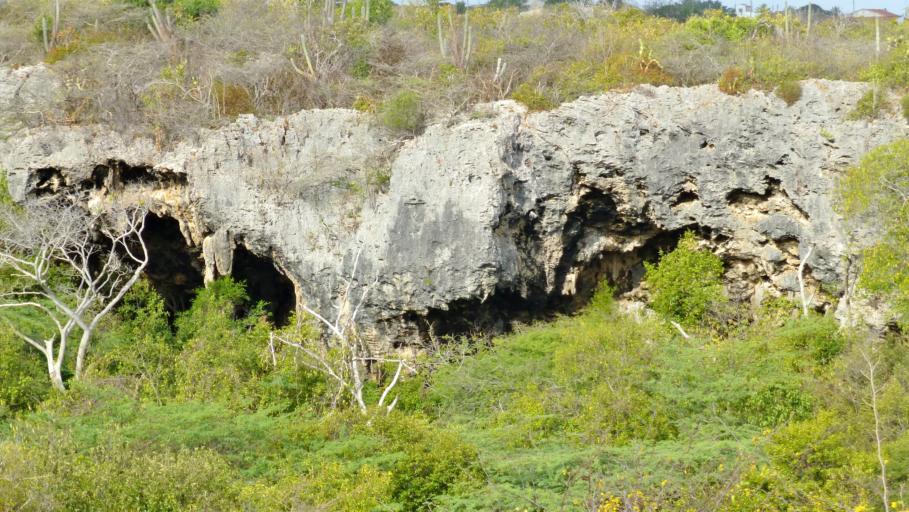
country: CW
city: Sint Michiel Liber
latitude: 12.1810
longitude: -68.9618
